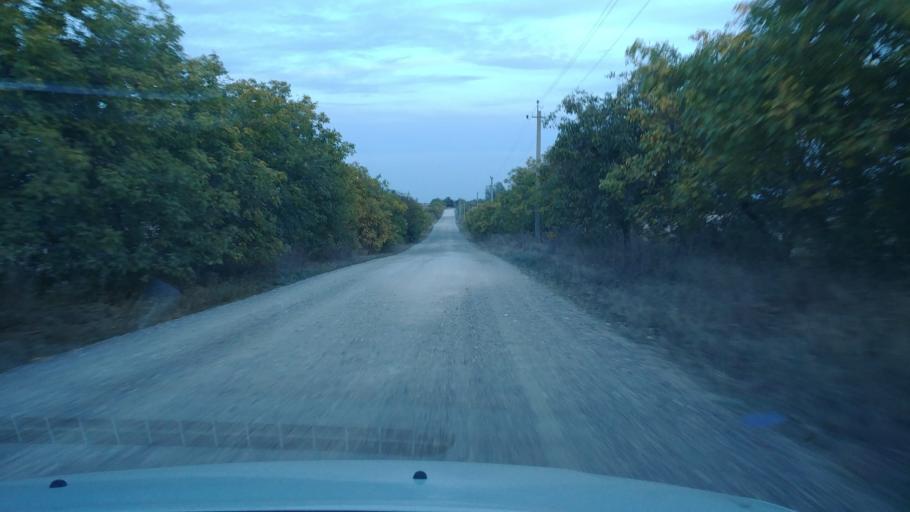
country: MD
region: Rezina
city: Saharna
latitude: 47.6813
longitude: 28.9088
